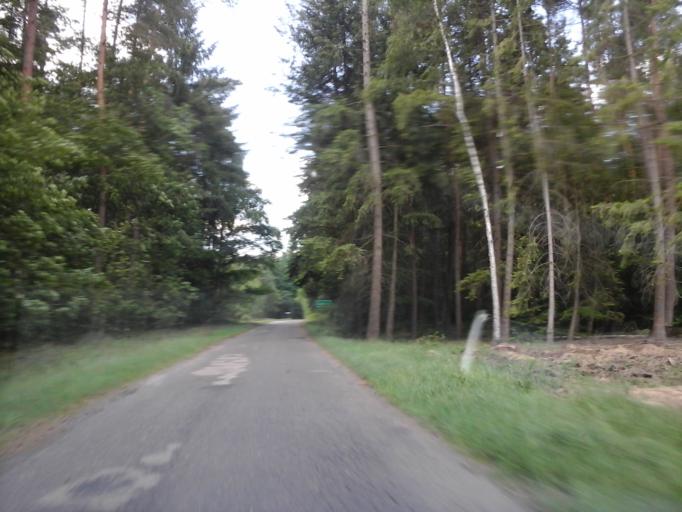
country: PL
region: West Pomeranian Voivodeship
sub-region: Powiat choszczenski
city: Bierzwnik
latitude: 53.1051
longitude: 15.7464
